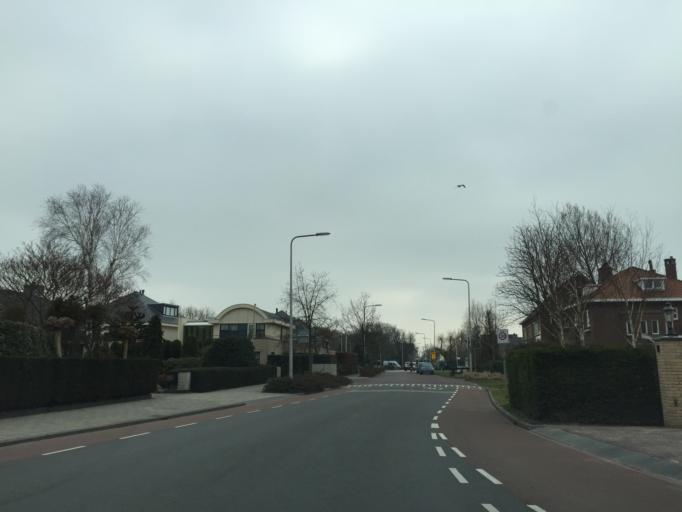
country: NL
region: South Holland
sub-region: Gemeente Westland
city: Naaldwijk
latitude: 51.9885
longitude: 4.2069
